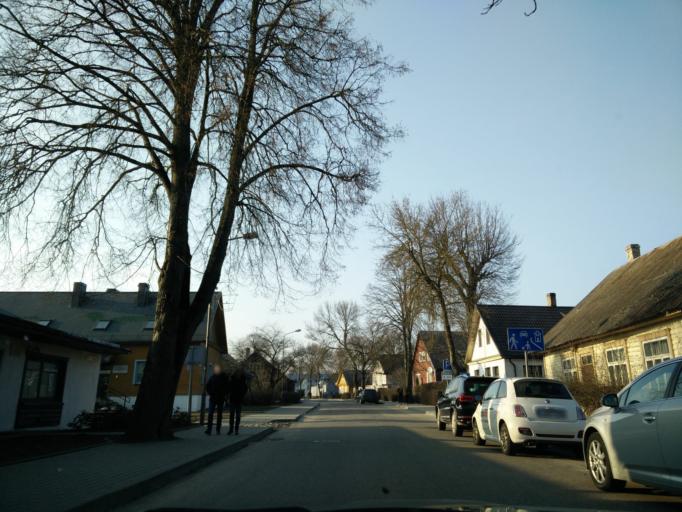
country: LT
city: Trakai
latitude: 54.6461
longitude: 24.9349
